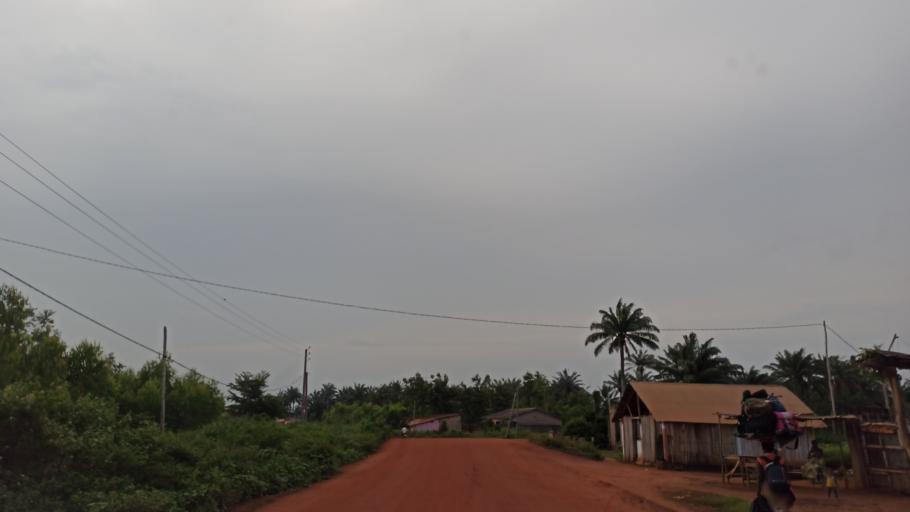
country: BJ
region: Queme
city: Porto-Novo
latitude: 6.5146
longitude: 2.6838
